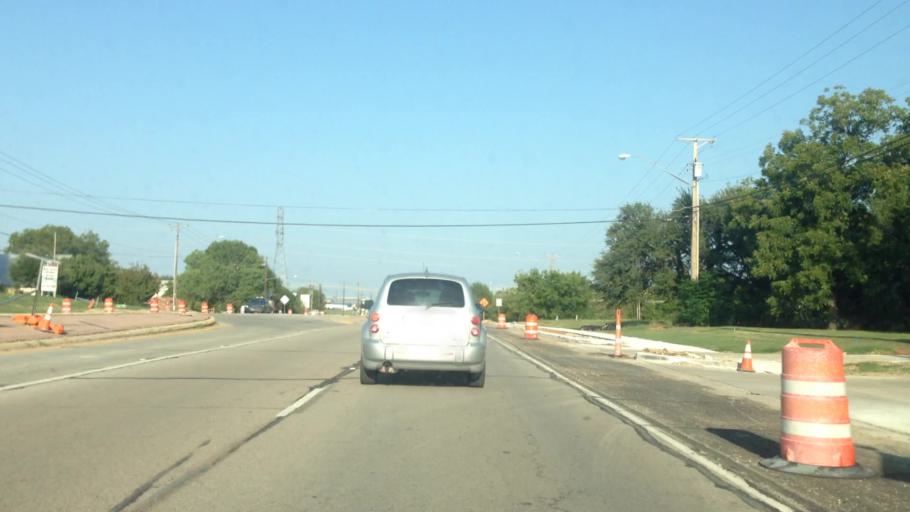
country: US
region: Texas
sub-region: Tarrant County
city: Richland Hills
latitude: 32.8090
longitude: -97.2252
